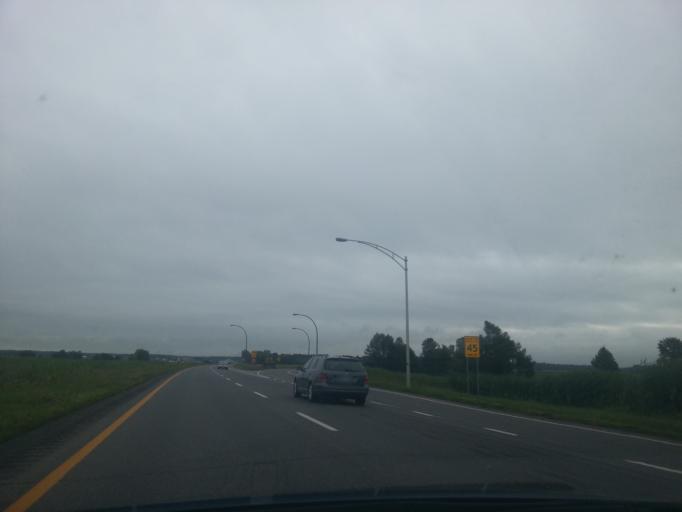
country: CA
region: Quebec
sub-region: Monteregie
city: Saint-Hyacinthe
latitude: 45.6499
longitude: -72.9440
